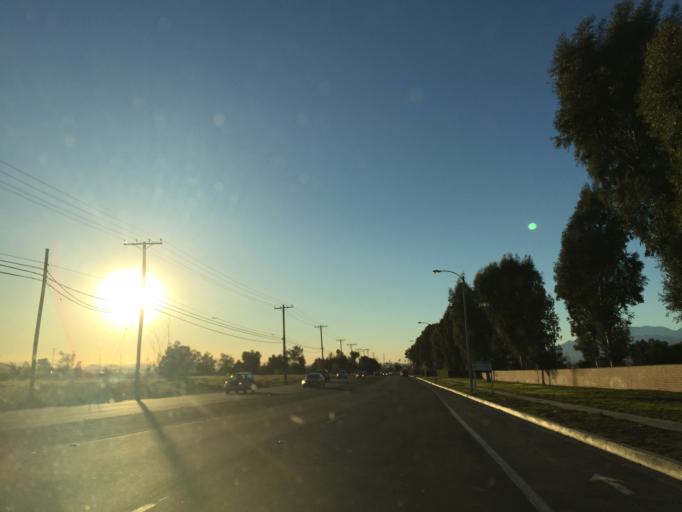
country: US
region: California
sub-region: San Bernardino County
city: Highland
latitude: 34.1084
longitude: -117.1780
